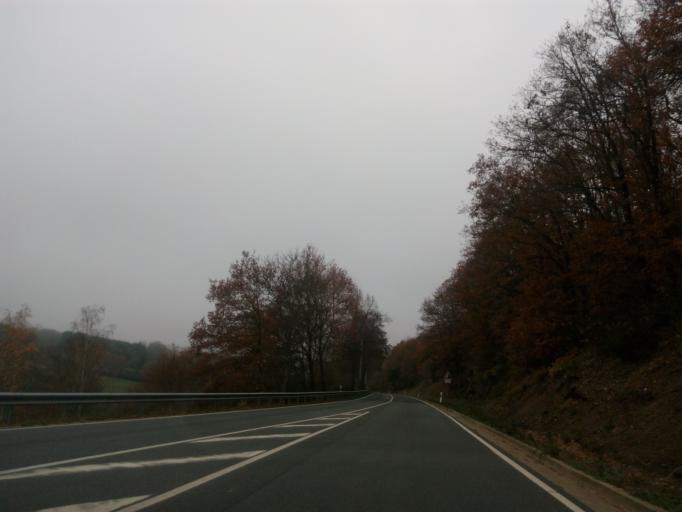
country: DE
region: Rheinland-Pfalz
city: Mittelreidenbach
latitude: 49.7332
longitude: 7.4394
